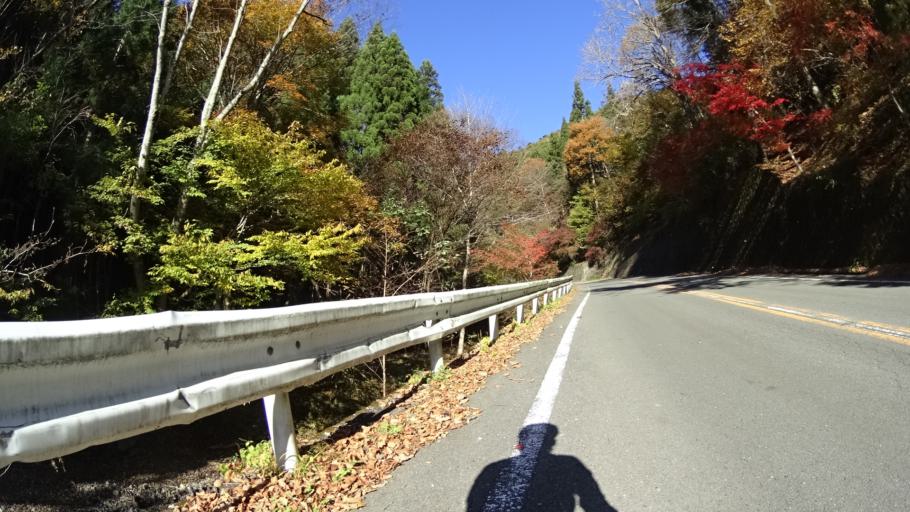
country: JP
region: Yamanashi
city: Otsuki
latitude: 35.7282
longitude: 138.9849
